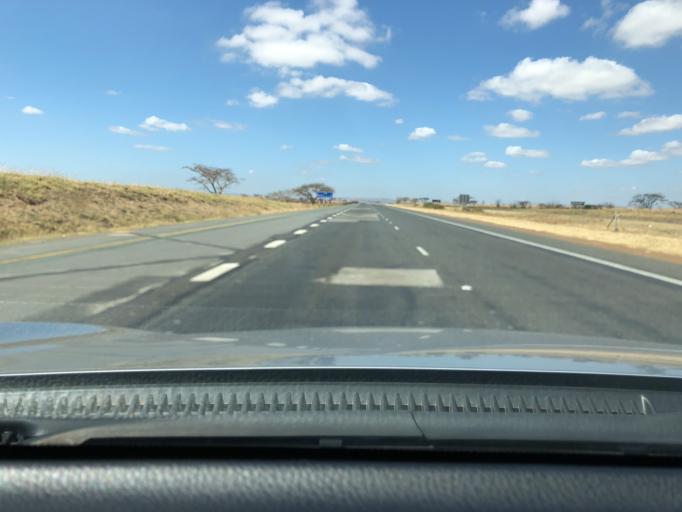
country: ZA
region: KwaZulu-Natal
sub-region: uThukela District Municipality
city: Estcourt
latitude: -28.9286
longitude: 29.7831
